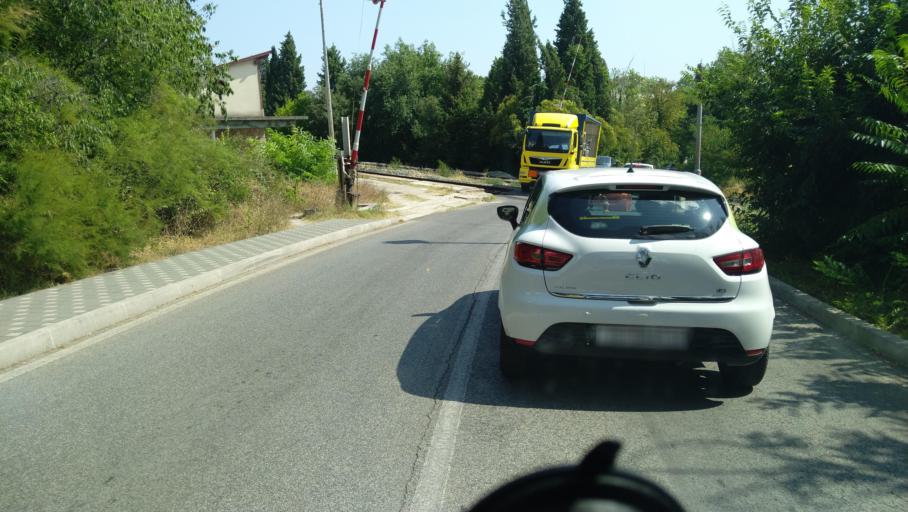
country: HR
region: Sibensko-Kniniska
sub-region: Grad Sibenik
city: Sibenik
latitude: 43.7205
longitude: 15.9067
